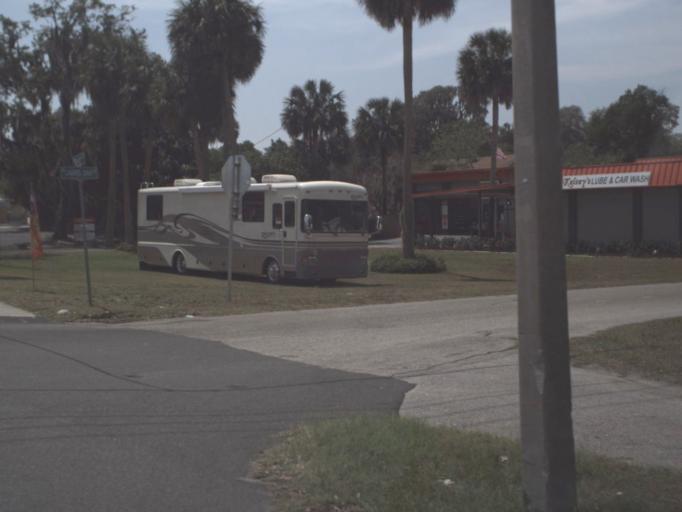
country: US
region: Florida
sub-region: Lake County
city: Eustis
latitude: 28.8637
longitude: -81.6866
